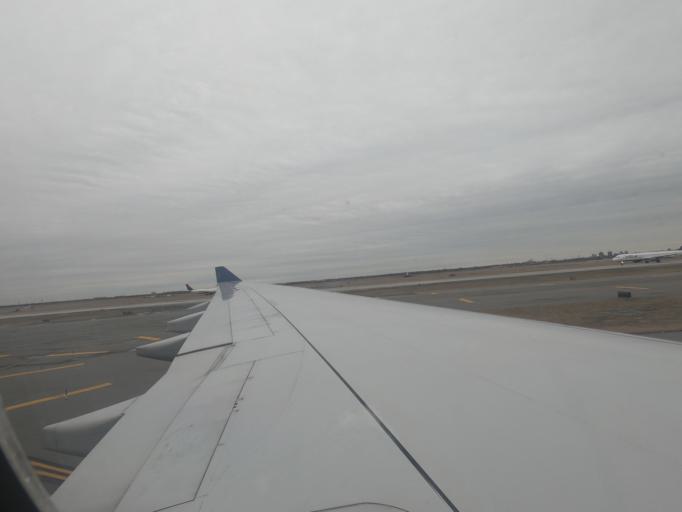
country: US
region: New York
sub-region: Nassau County
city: Inwood
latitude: 40.6365
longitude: -73.7771
